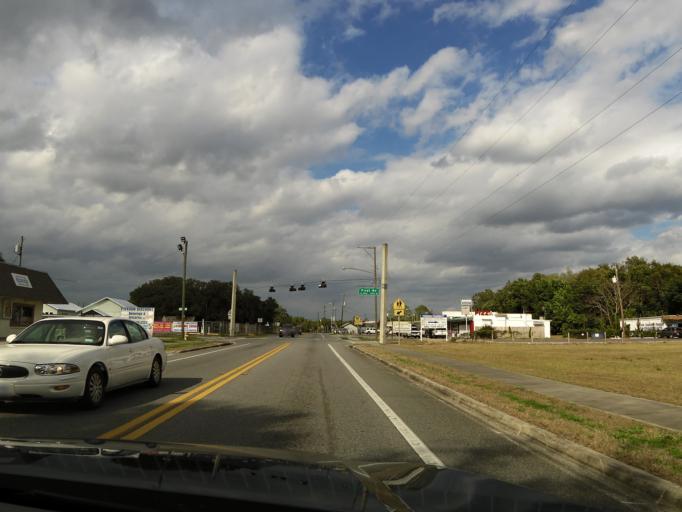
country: US
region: Florida
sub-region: Volusia County
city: Pierson
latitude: 29.2428
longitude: -81.4630
